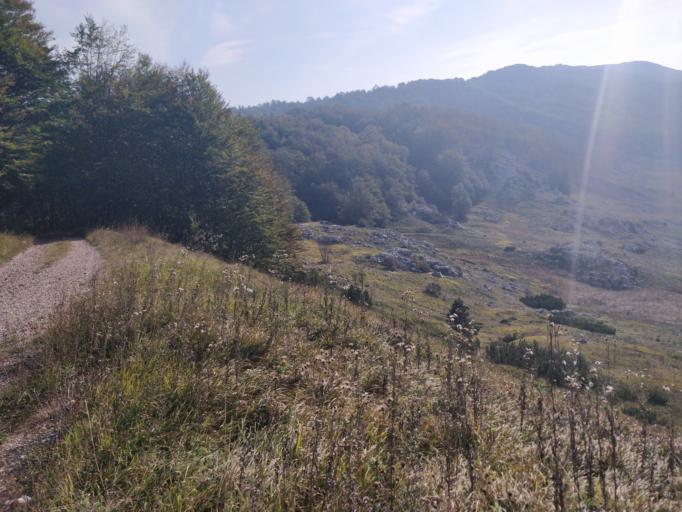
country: HR
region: Zadarska
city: Starigrad
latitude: 44.3628
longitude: 15.5331
